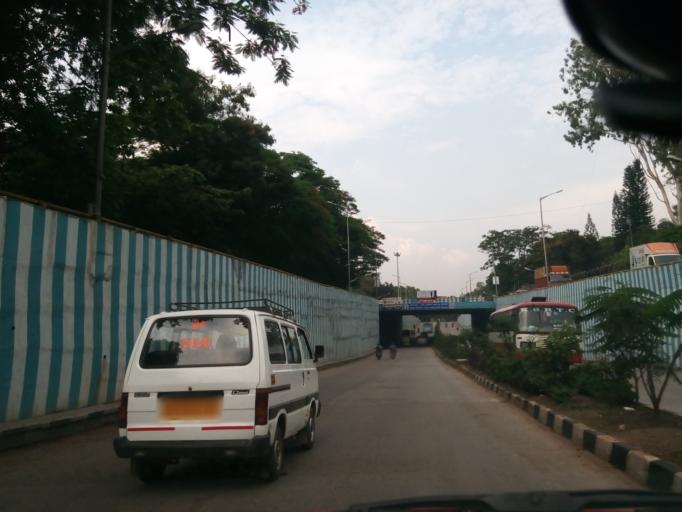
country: IN
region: Karnataka
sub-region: Bangalore Urban
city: Bangalore
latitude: 13.0148
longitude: 77.5648
